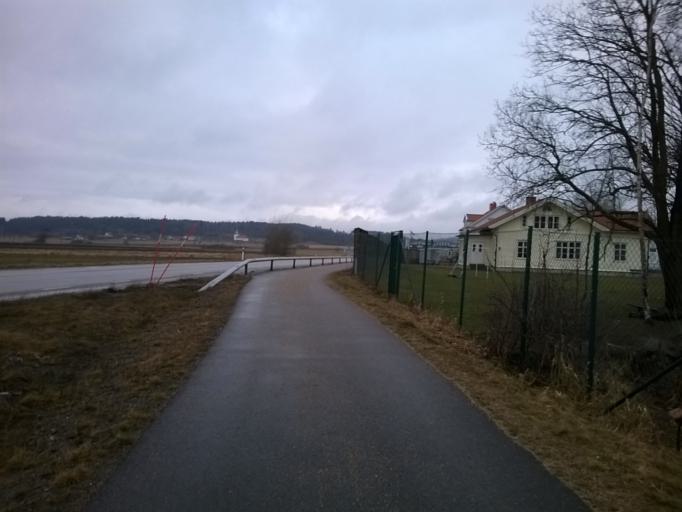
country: SE
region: Vaestra Goetaland
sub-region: Kungalvs Kommun
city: Kungalv
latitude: 57.9033
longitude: 11.9267
